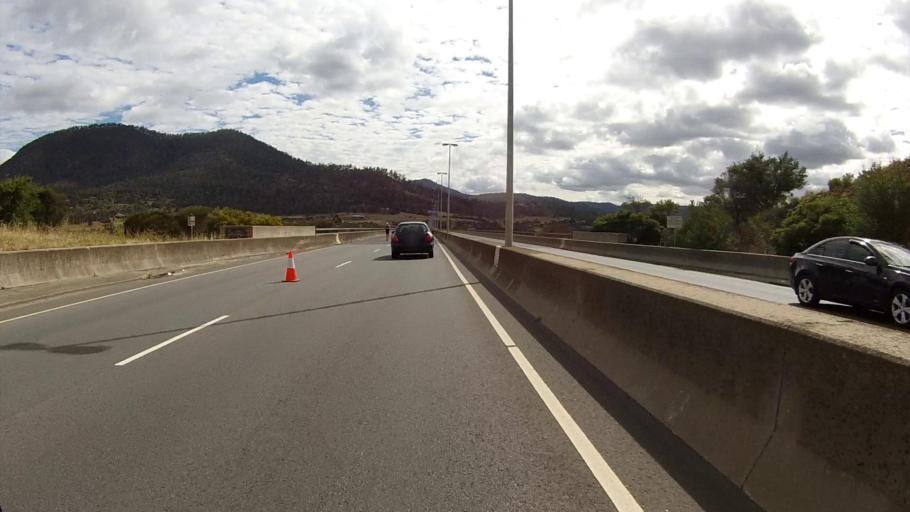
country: AU
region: Tasmania
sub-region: Glenorchy
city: Goodwood
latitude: -42.8211
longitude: 147.3030
